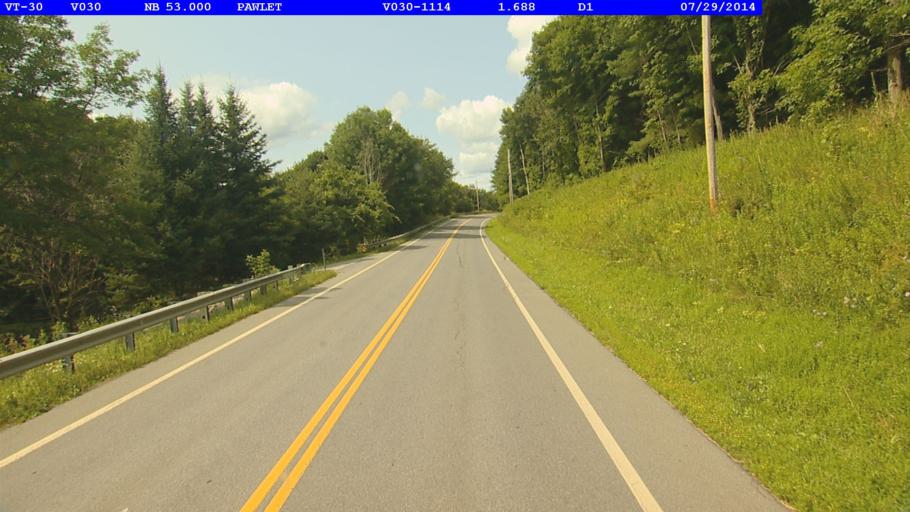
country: US
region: New York
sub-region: Washington County
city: Granville
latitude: 43.3344
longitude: -73.1766
